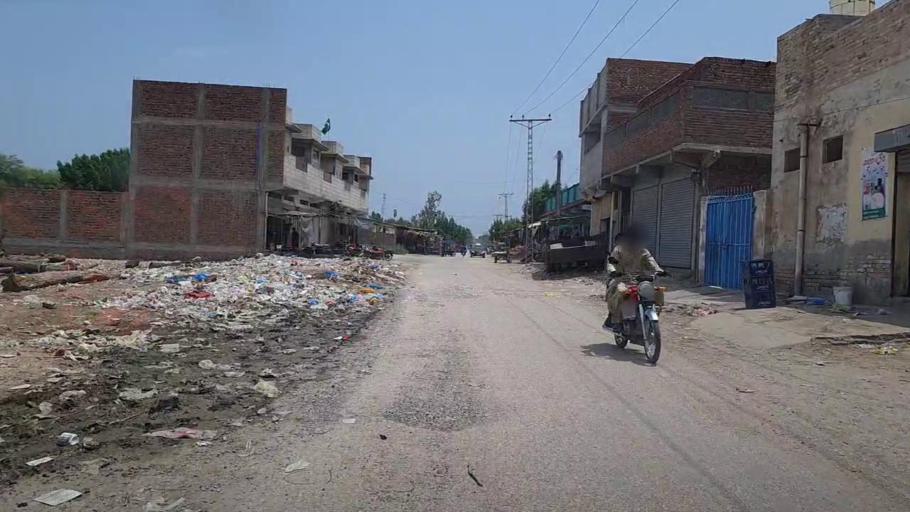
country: PK
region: Sindh
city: Khairpur
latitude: 28.0533
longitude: 69.6921
